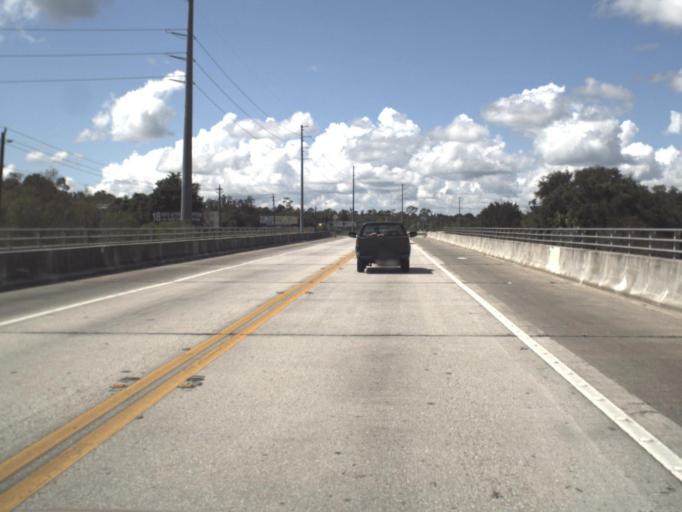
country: US
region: Florida
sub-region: DeSoto County
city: Arcadia
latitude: 27.2233
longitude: -81.8828
